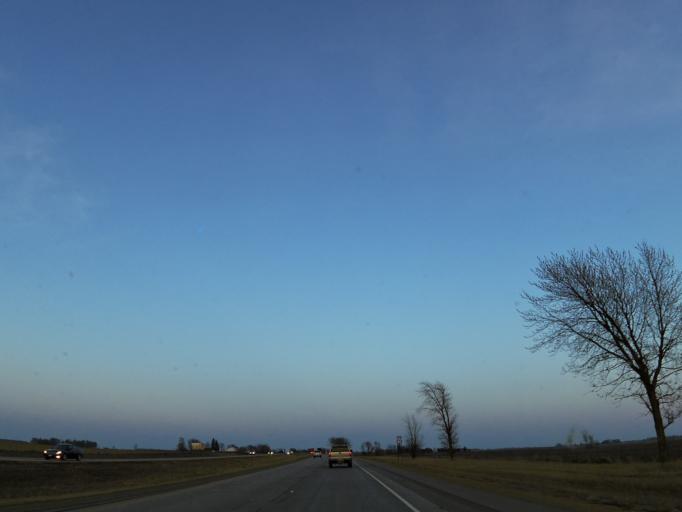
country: US
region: Minnesota
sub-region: Mower County
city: Austin
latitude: 43.6715
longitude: -92.8621
